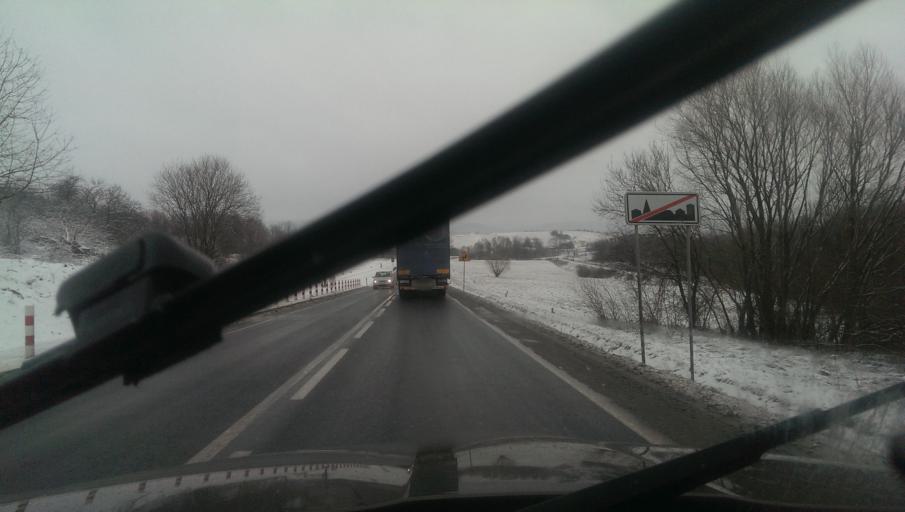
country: PL
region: Subcarpathian Voivodeship
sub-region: Powiat sanocki
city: Nowosielce-Gniewosz
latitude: 49.5610
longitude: 22.1140
